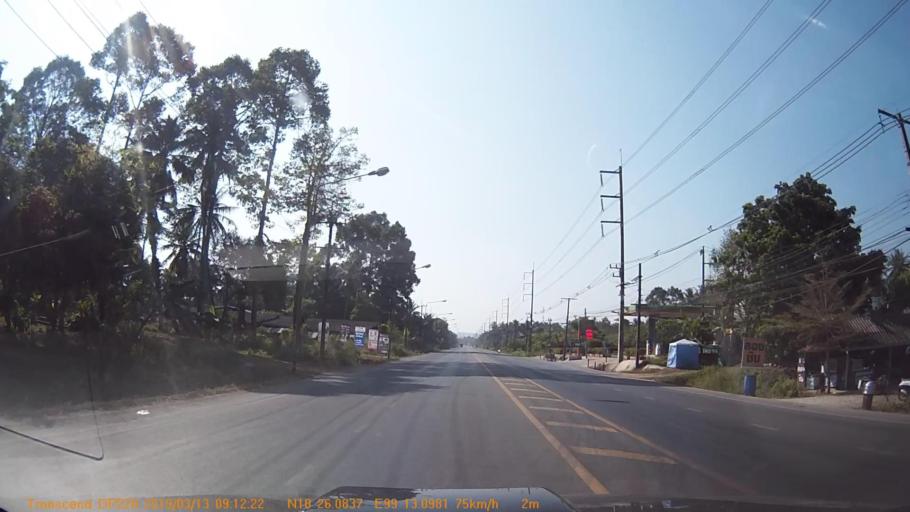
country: TH
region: Chumphon
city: Chumphon
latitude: 10.4345
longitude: 99.2184
